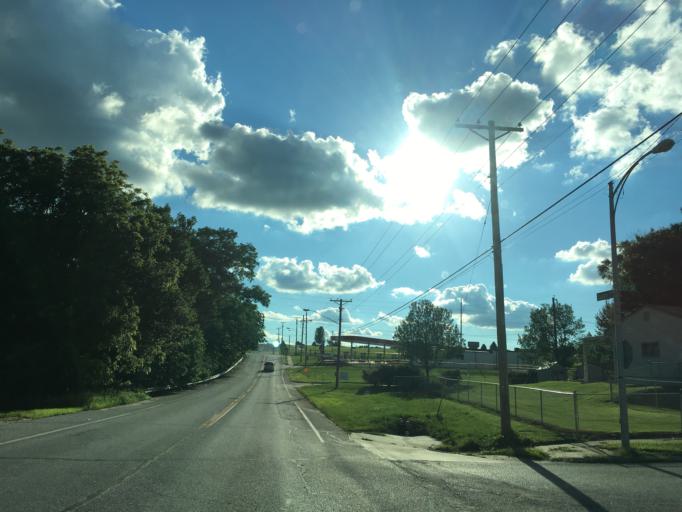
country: US
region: Nebraska
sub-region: Sarpy County
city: La Vista
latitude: 41.1836
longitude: -95.9650
